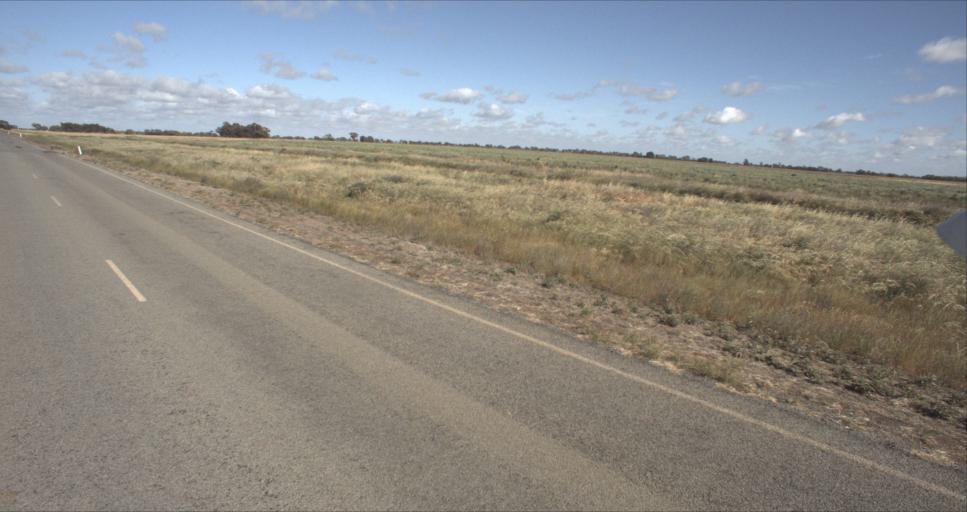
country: AU
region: New South Wales
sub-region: Leeton
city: Leeton
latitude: -34.5533
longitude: 146.2929
